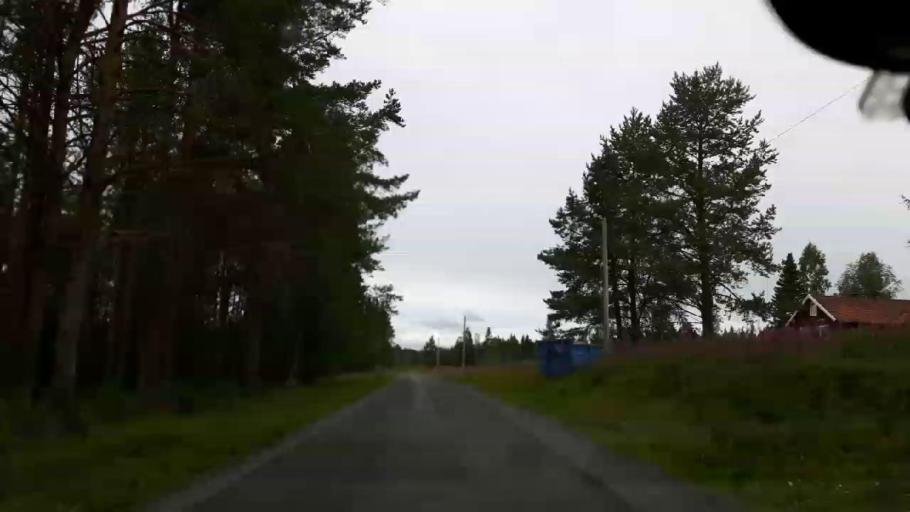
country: SE
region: Jaemtland
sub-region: Krokoms Kommun
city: Krokom
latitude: 63.2754
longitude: 14.3994
